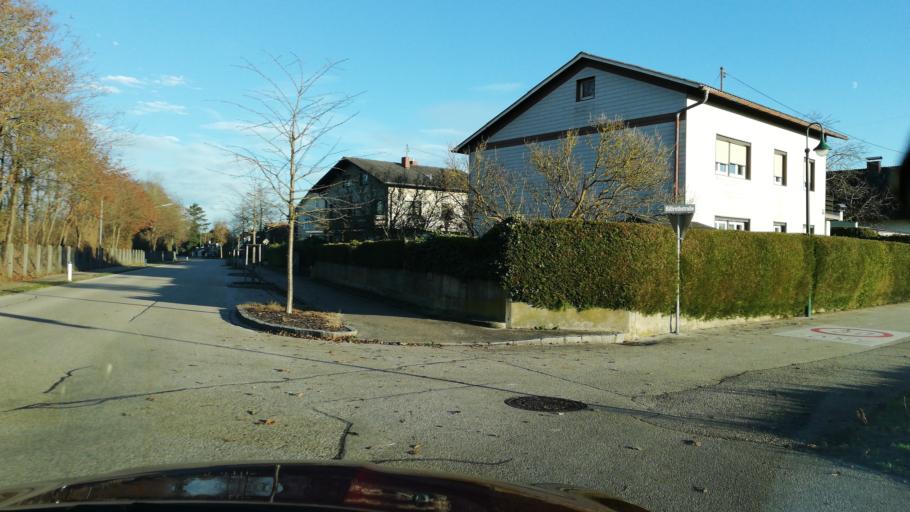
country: AT
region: Upper Austria
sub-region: Politischer Bezirk Linz-Land
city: Traun
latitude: 48.2325
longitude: 14.2428
